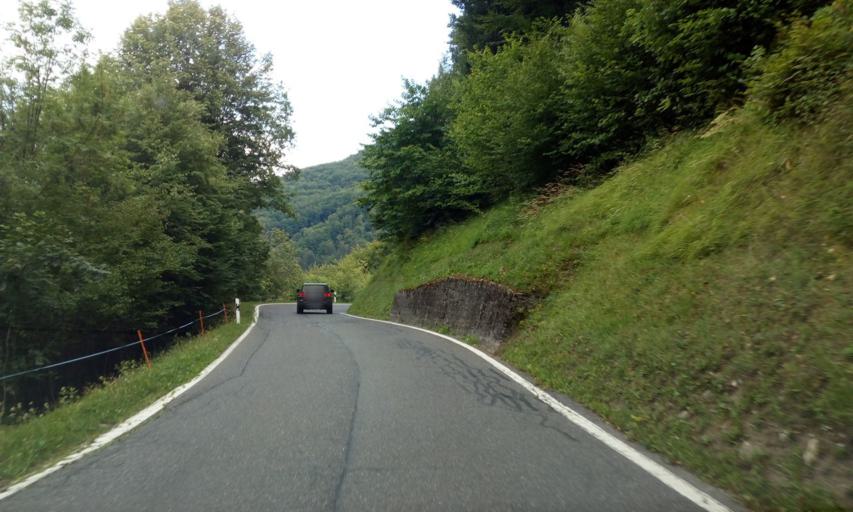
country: CH
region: Valais
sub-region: Monthey District
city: Vionnaz
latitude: 46.3077
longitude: 6.8876
